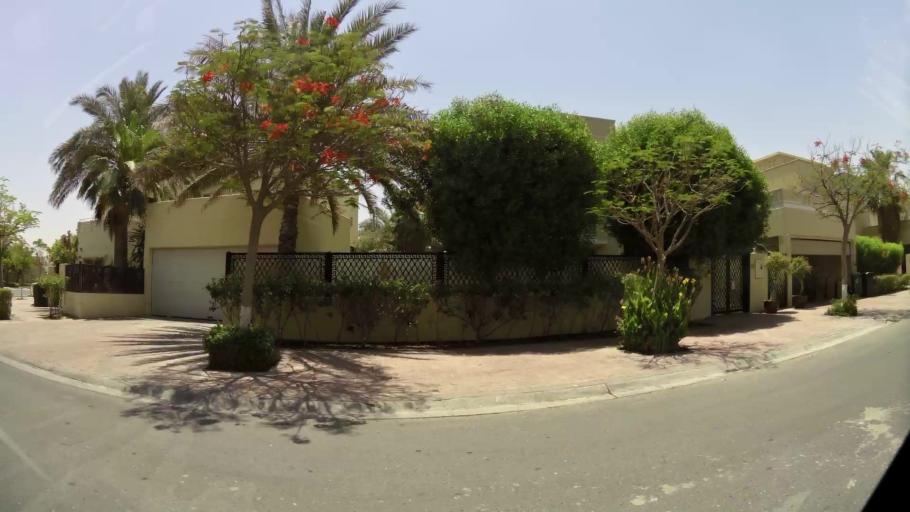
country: AE
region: Dubai
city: Dubai
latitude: 25.0467
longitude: 55.1728
